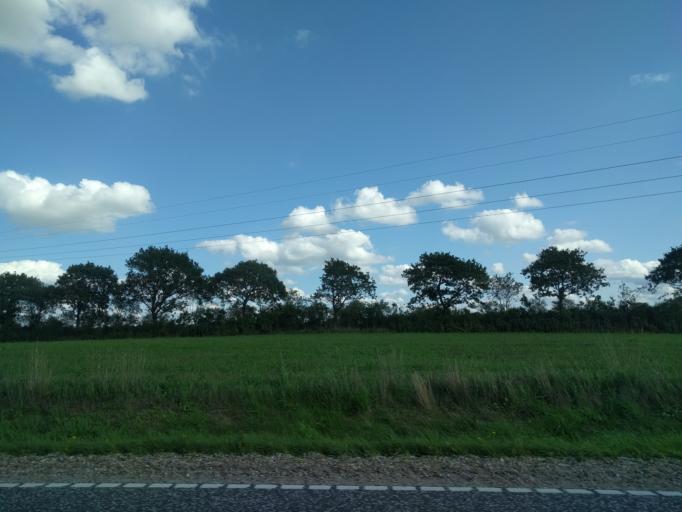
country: DK
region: Central Jutland
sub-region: Skive Kommune
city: Skive
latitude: 56.4720
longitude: 8.9588
